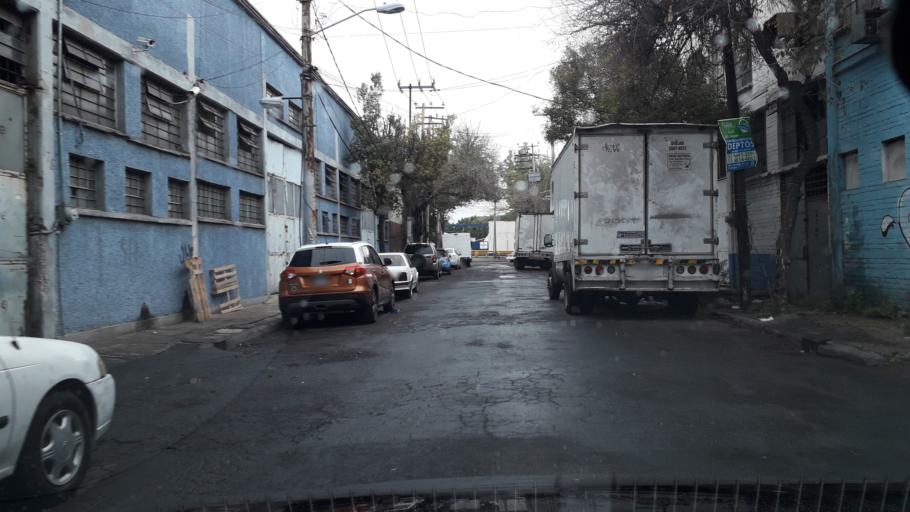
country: MX
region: Mexico City
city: Cuauhtemoc
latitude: 19.4618
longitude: -99.1544
